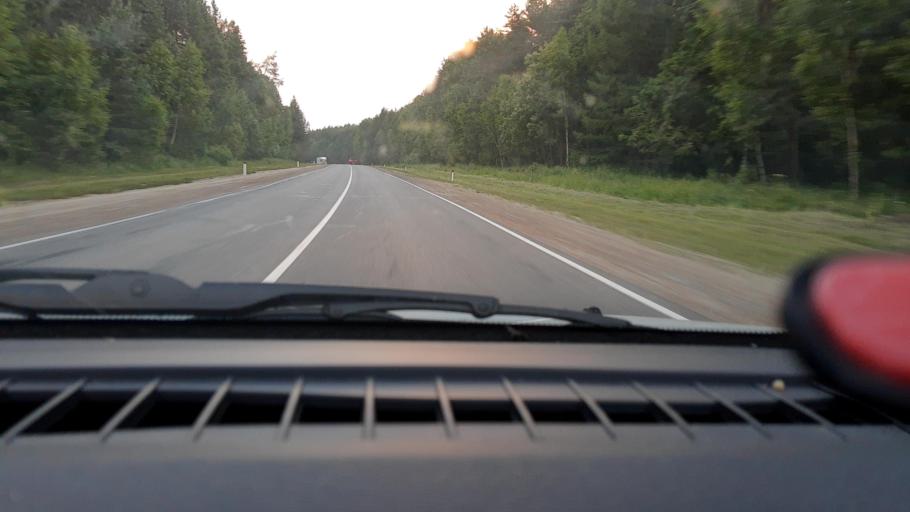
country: RU
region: Nizjnij Novgorod
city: Arzamas
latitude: 55.3773
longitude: 43.9141
